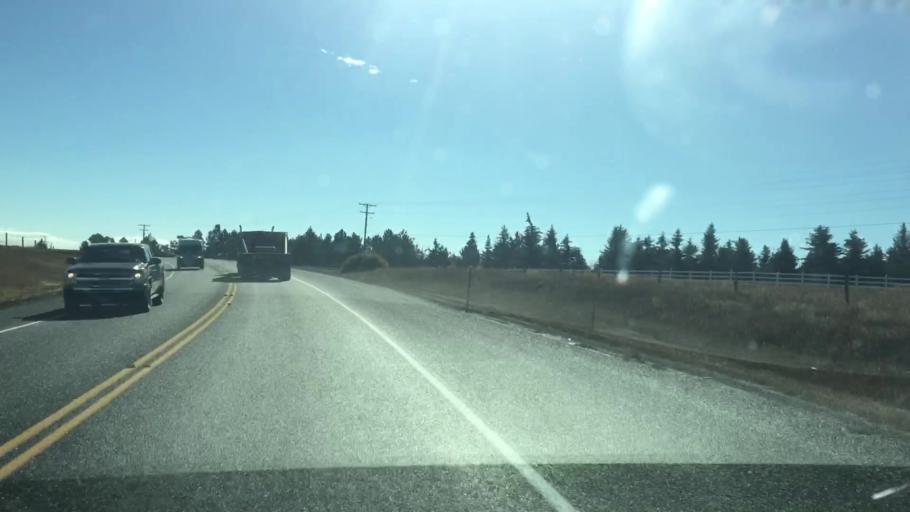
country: US
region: Colorado
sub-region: Elbert County
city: Ponderosa Park
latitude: 39.3625
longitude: -104.6704
